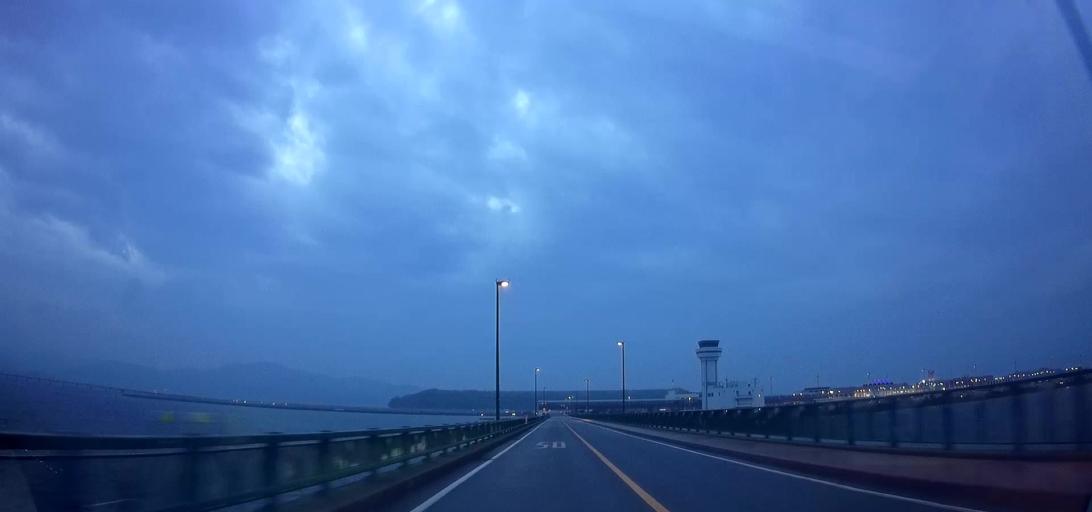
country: JP
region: Nagasaki
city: Omura
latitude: 32.9154
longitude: 129.9289
